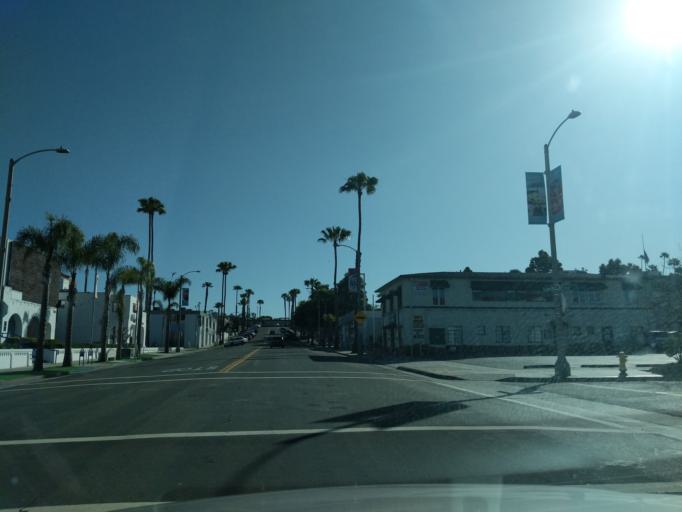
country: US
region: California
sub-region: San Diego County
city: Oceanside
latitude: 33.1976
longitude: -117.3789
